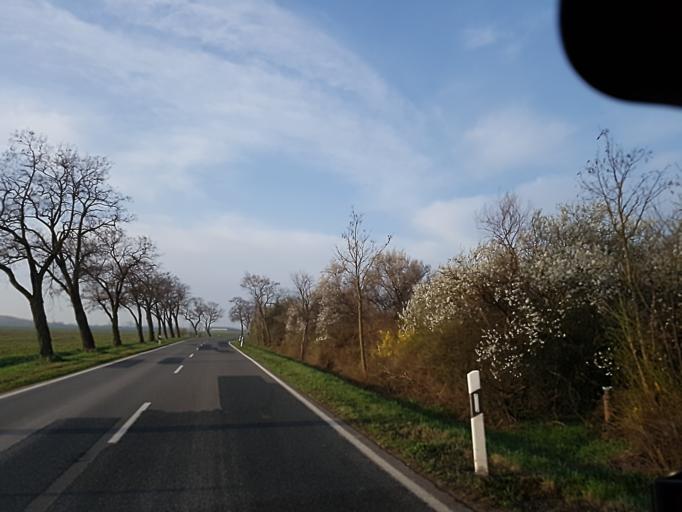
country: DE
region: Brandenburg
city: Muhlberg
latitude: 51.4340
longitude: 13.2693
